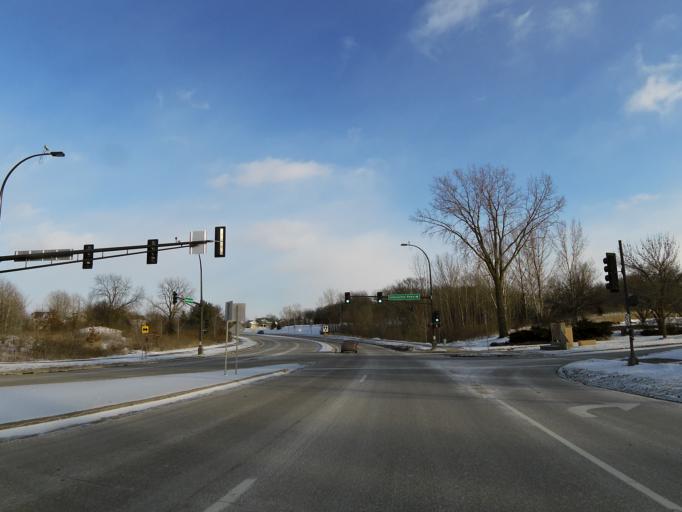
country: US
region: Minnesota
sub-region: Washington County
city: Woodbury
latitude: 44.9382
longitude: -92.9200
